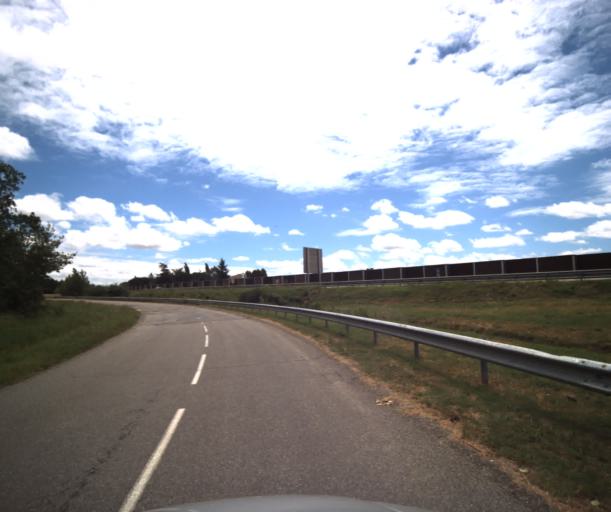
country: FR
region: Midi-Pyrenees
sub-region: Departement de la Haute-Garonne
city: Lacroix-Falgarde
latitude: 43.4828
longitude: 1.4032
